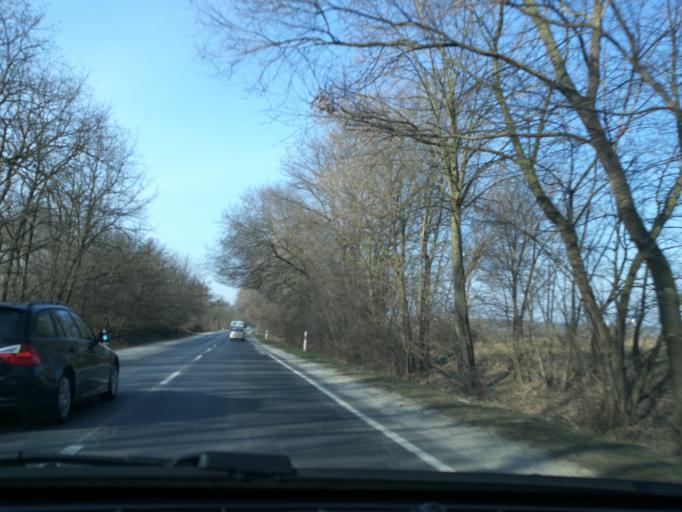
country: HU
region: Szabolcs-Szatmar-Bereg
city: Apagy
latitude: 47.9553
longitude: 21.9070
